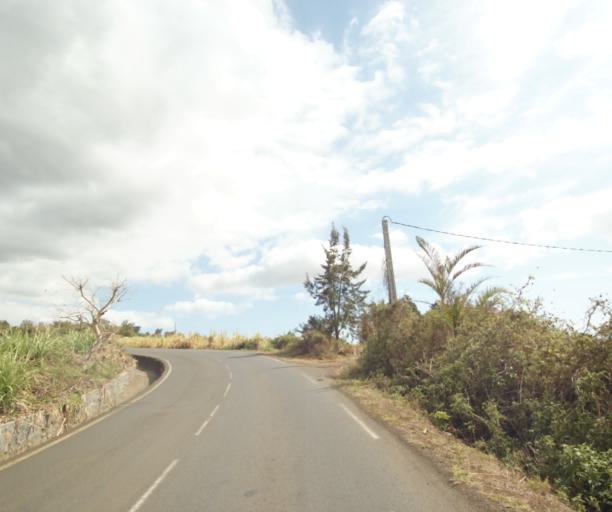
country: RE
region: Reunion
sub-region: Reunion
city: Saint-Paul
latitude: -21.0323
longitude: 55.2862
